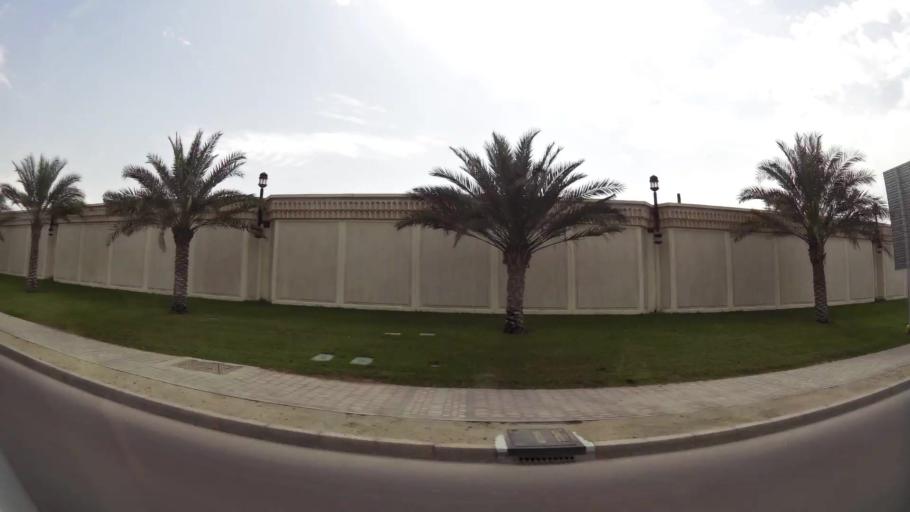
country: AE
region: Abu Dhabi
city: Abu Dhabi
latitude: 24.4554
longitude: 54.3452
